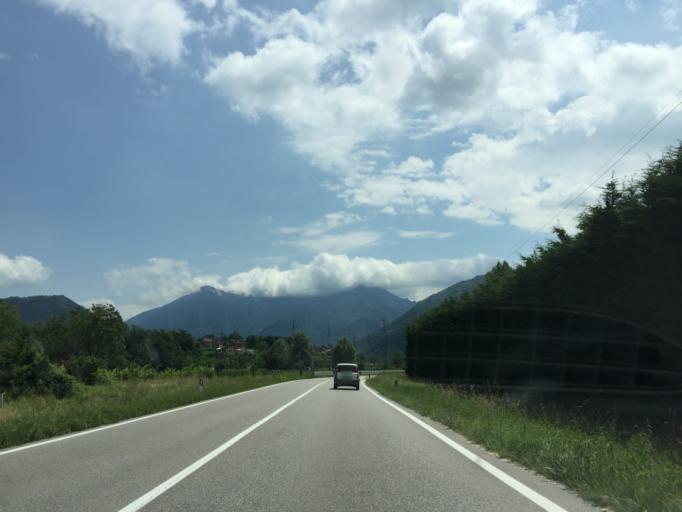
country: IT
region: Veneto
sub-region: Provincia di Belluno
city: Fonzaso
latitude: 46.0161
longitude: 11.7900
